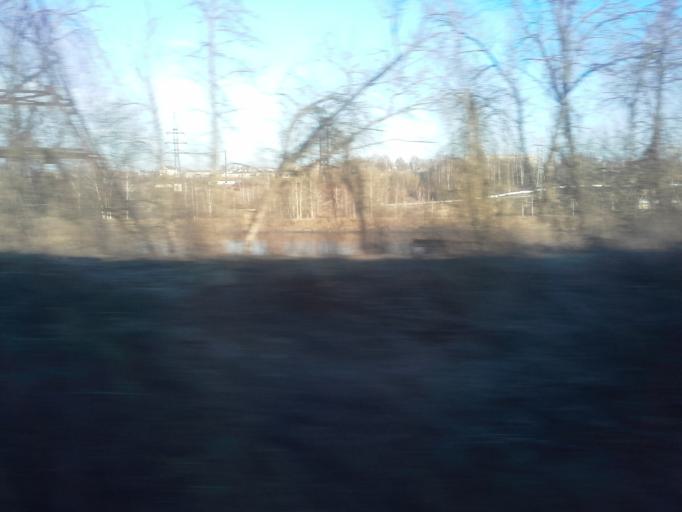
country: RU
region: Moskovskaya
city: Iksha
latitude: 56.1794
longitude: 37.5157
